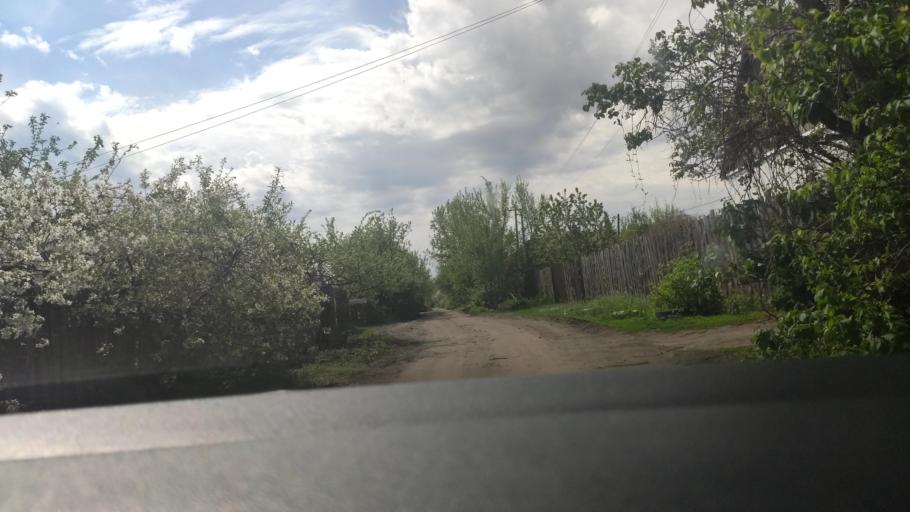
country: RU
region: Voronezj
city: Maslovka
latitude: 51.6066
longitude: 39.2790
